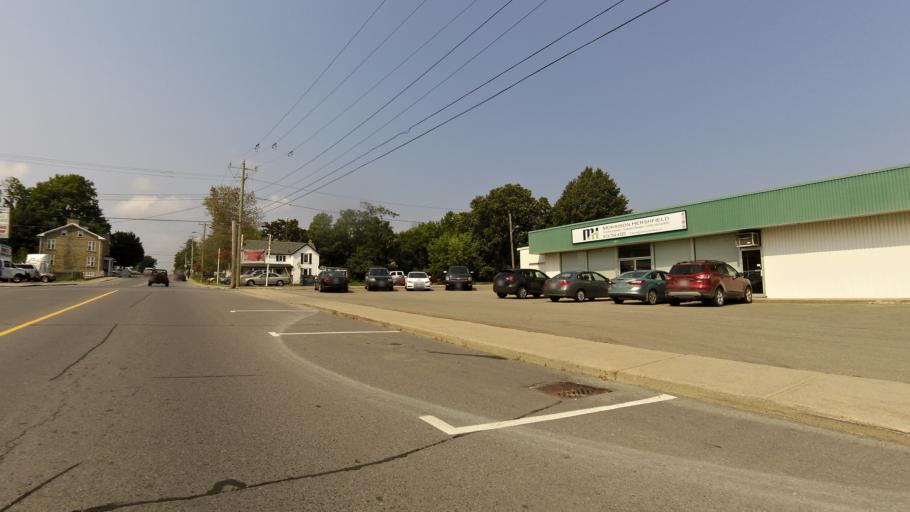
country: CA
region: Ontario
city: Prescott
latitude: 44.7108
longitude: -75.5133
